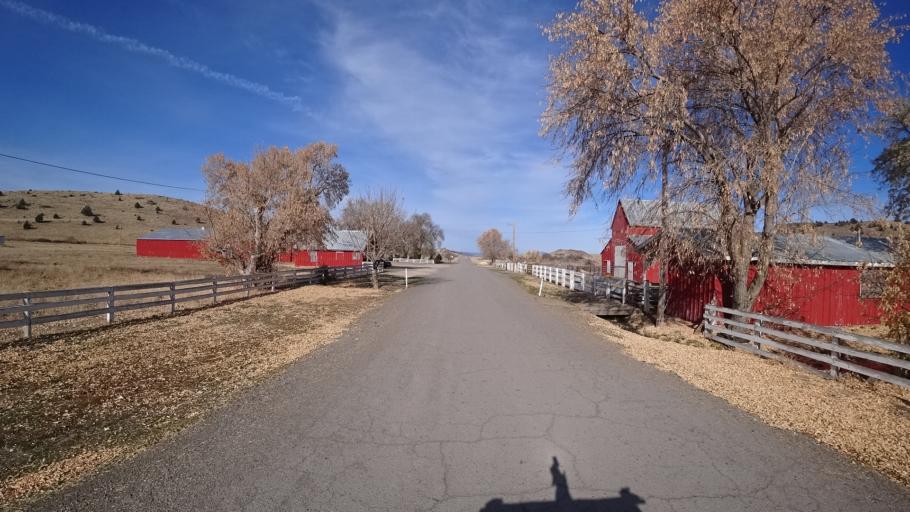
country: US
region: California
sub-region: Siskiyou County
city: Weed
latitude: 41.5019
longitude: -122.4548
